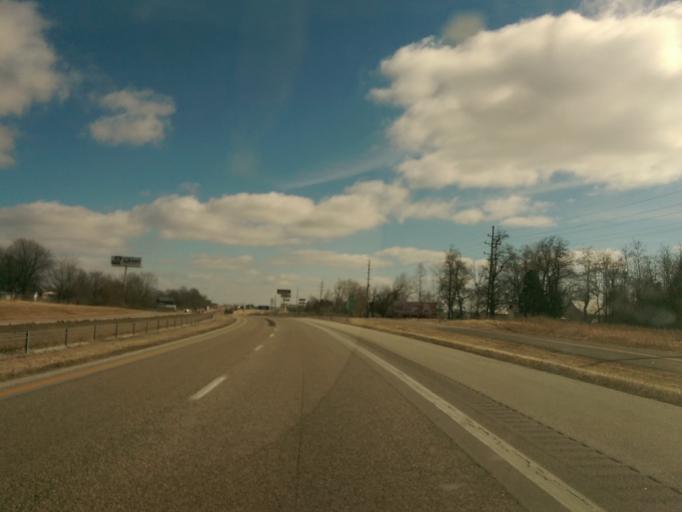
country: US
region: Missouri
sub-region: Montgomery County
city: Montgomery City
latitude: 38.8782
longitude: -91.3870
